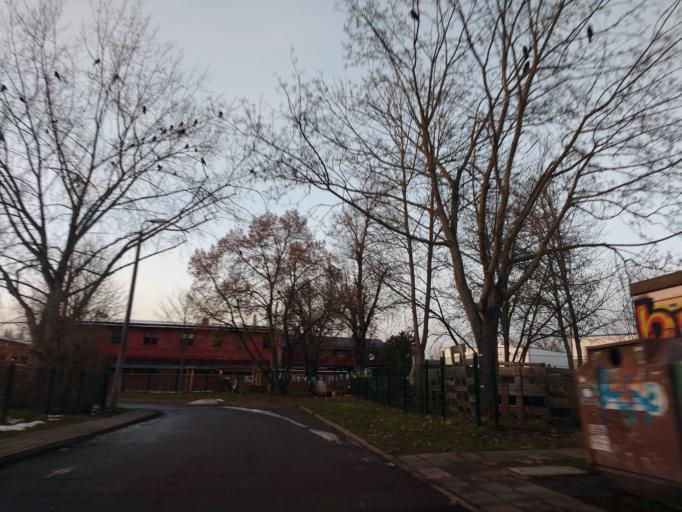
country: DE
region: Saxony-Anhalt
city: Sennewitz
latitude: 51.5220
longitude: 11.9597
